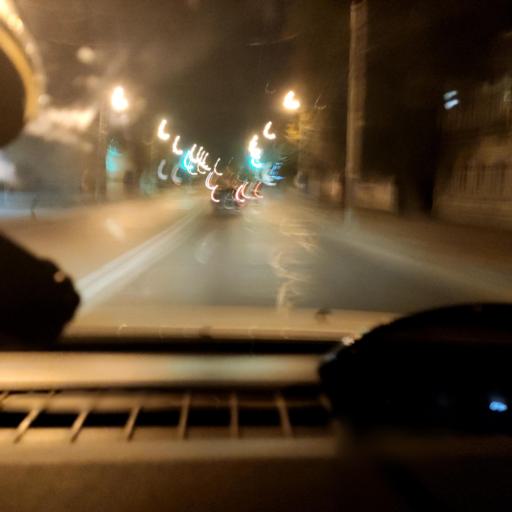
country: RU
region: Samara
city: Rozhdestveno
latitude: 53.1688
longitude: 50.0752
